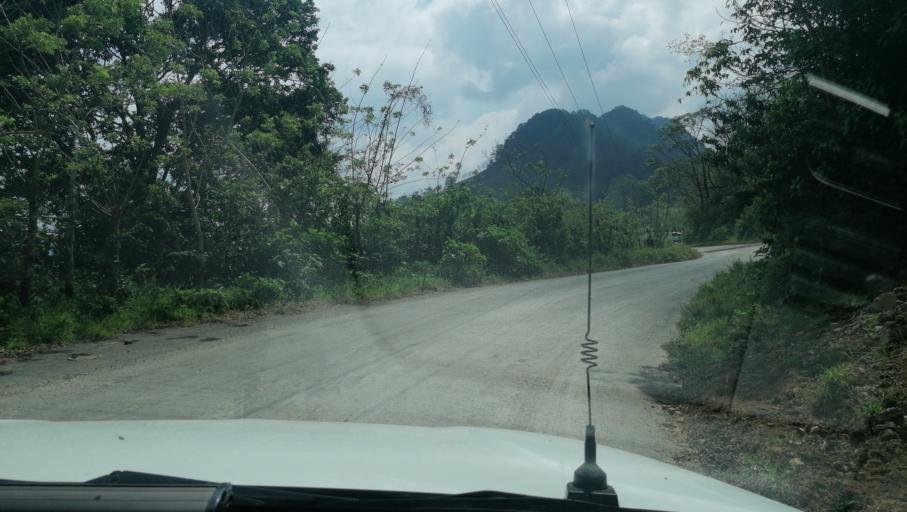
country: MX
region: Chiapas
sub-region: Francisco Leon
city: San Miguel la Sardina
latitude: 17.2529
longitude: -93.2759
